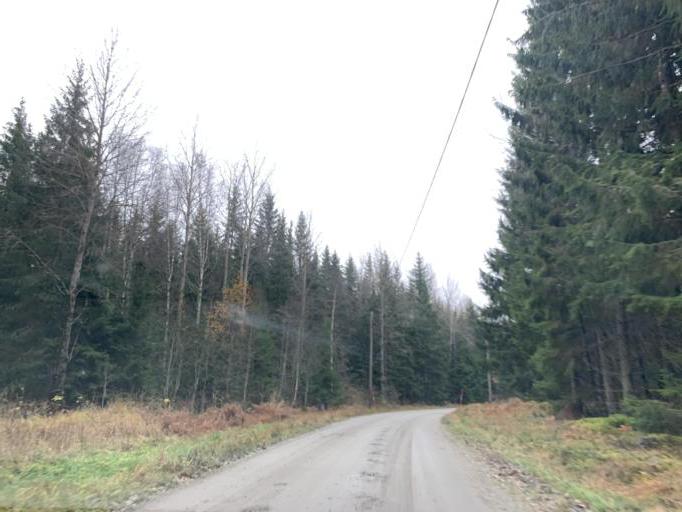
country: SE
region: Vaestmanland
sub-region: Surahammars Kommun
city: Ramnas
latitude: 59.7152
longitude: 16.0946
